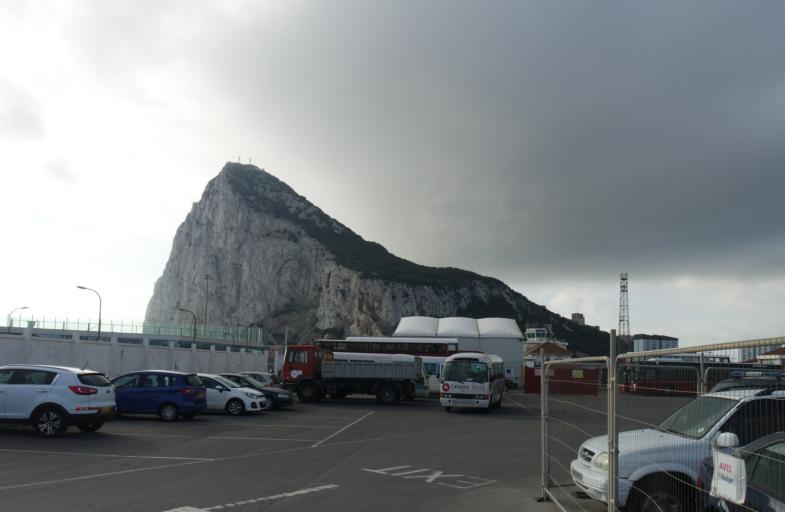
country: GI
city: Gibraltar
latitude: 36.1541
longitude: -5.3479
